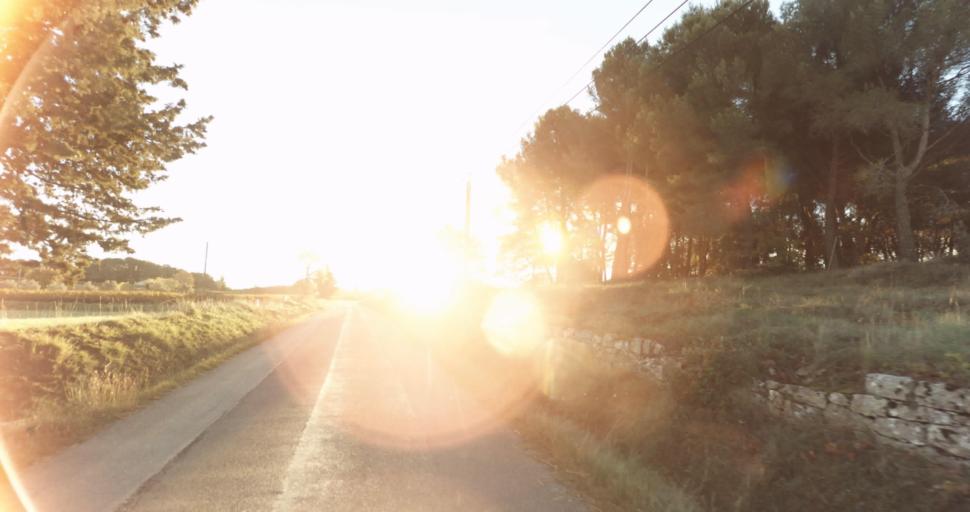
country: FR
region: Provence-Alpes-Cote d'Azur
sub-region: Departement des Bouches-du-Rhone
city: Venelles
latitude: 43.5784
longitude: 5.4783
